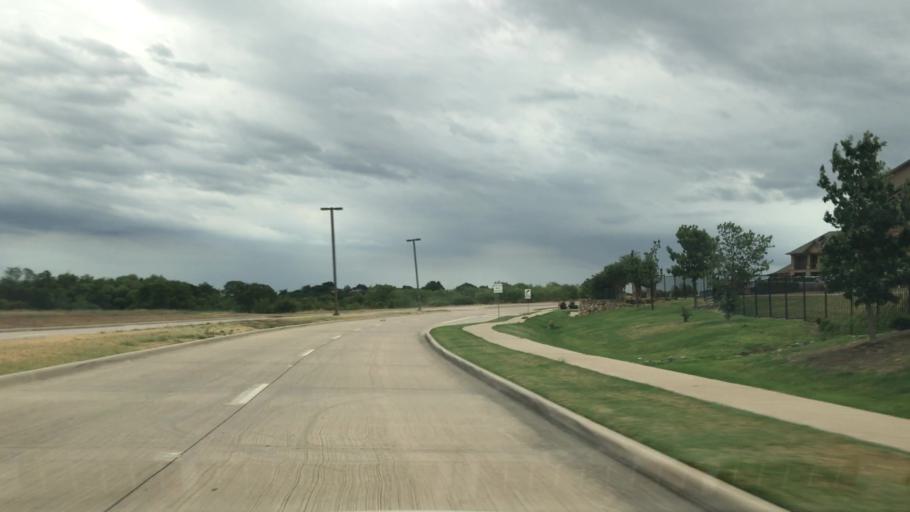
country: US
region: Texas
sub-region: Dallas County
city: Carrollton
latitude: 32.9885
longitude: -96.9056
